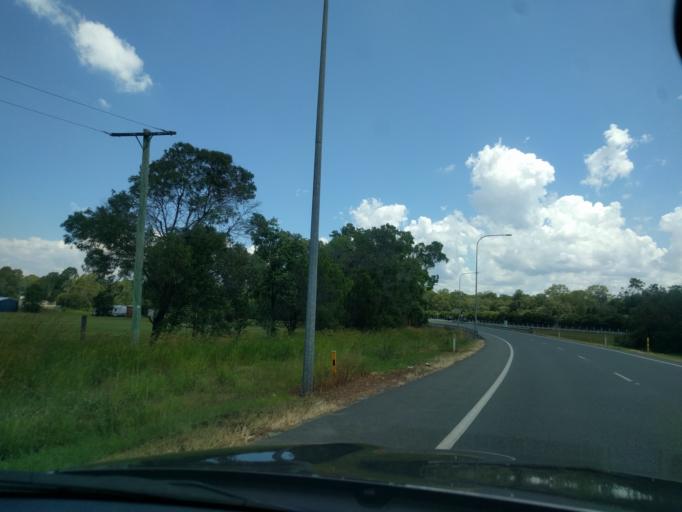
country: AU
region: Queensland
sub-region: Moreton Bay
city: Burpengary
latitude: -27.1413
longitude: 152.9792
